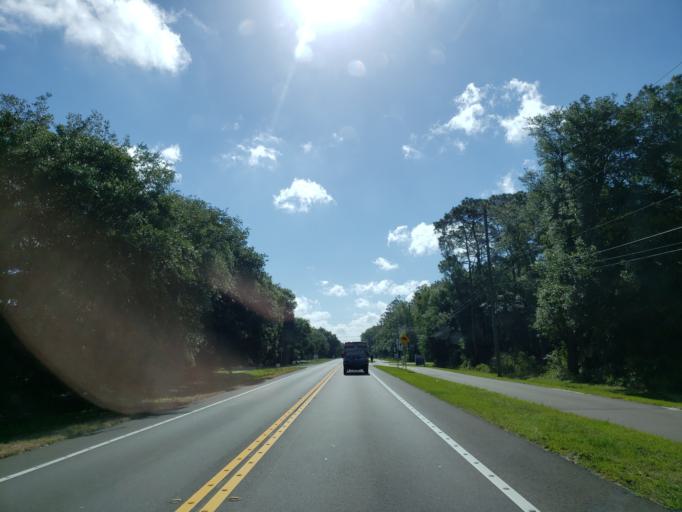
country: US
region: Florida
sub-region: Pasco County
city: Trinity
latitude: 28.1447
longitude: -82.6781
